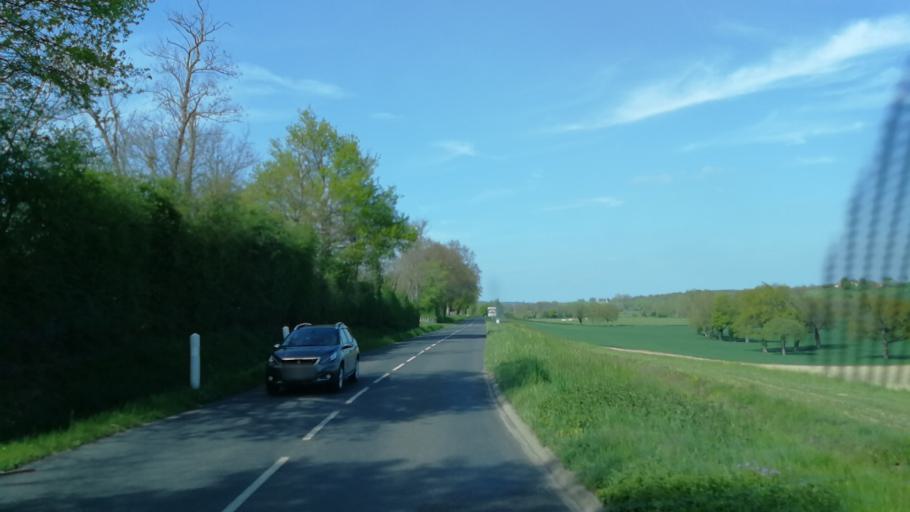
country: FR
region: Auvergne
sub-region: Departement de l'Allier
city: Saint-Gerand-le-Puy
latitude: 46.3596
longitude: 3.5767
